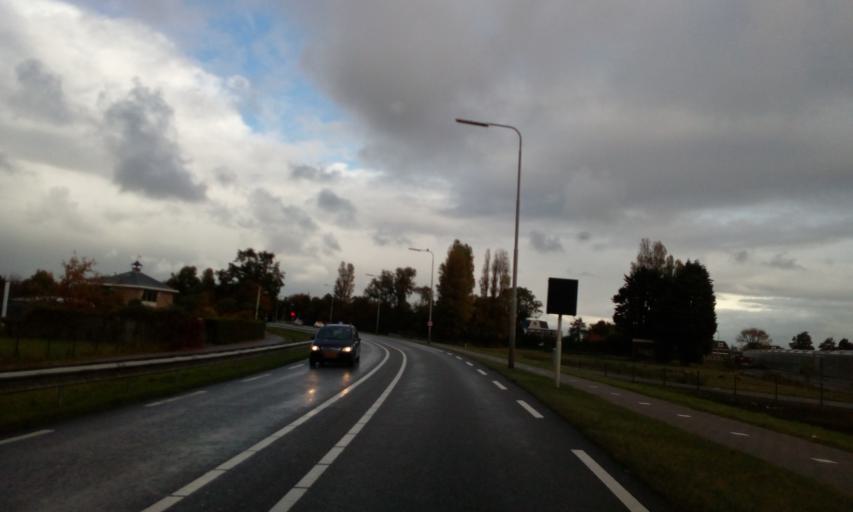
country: NL
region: South Holland
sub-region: Gemeente Westland
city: Honselersdijk
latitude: 52.0094
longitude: 4.2148
